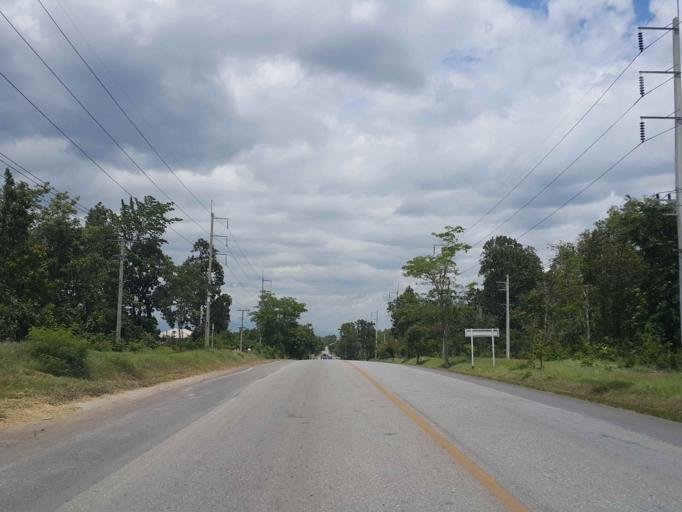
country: TH
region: Lamphun
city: Ban Hong
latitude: 18.3698
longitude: 98.8134
